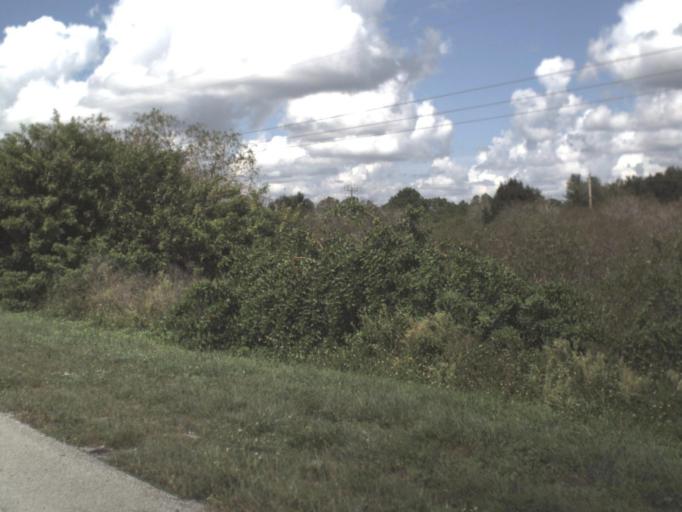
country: US
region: Florida
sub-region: Lee County
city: Gateway
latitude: 26.5771
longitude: -81.7030
